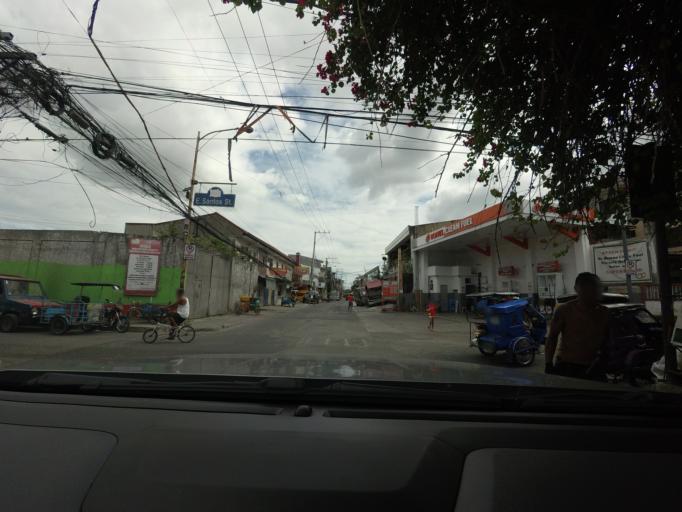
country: PH
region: Calabarzon
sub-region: Province of Rizal
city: Pateros
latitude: 14.5615
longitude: 121.0862
